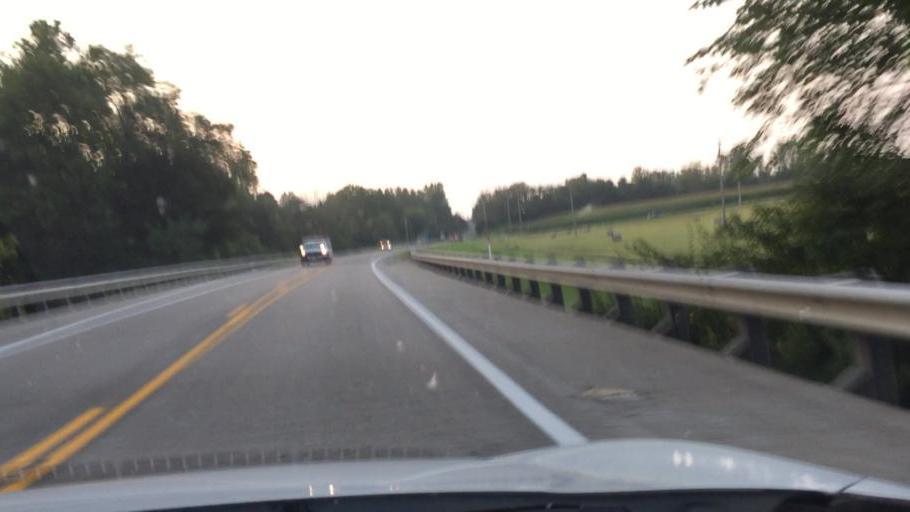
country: US
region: Ohio
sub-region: Madison County
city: Choctaw Lake
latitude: 39.9460
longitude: -83.5021
